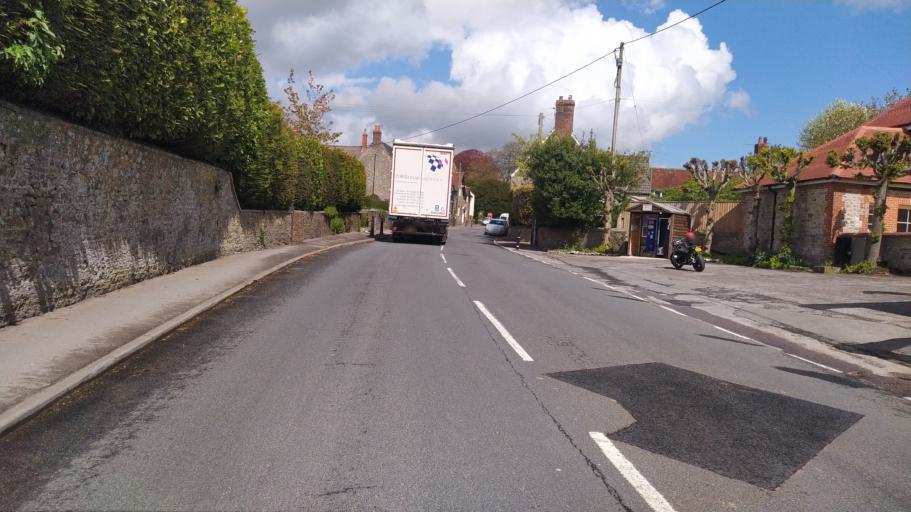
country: GB
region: England
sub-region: Wiltshire
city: Kilmington
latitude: 51.1484
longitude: -2.2851
